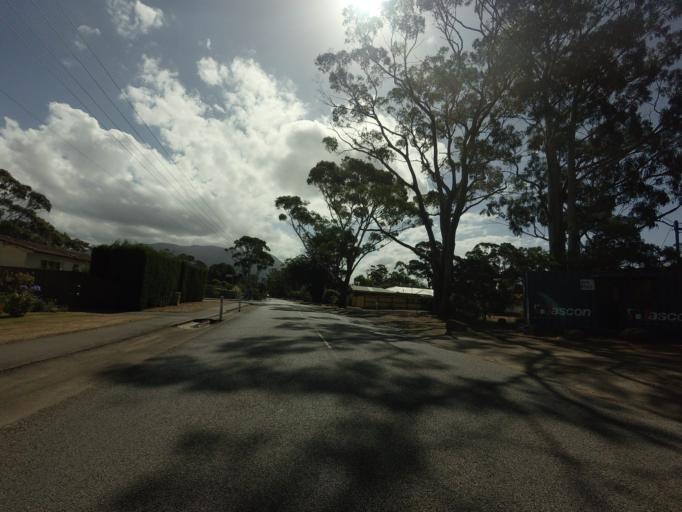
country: AU
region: Tasmania
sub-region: Hobart
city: Dynnyrne
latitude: -42.9246
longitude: 147.3283
